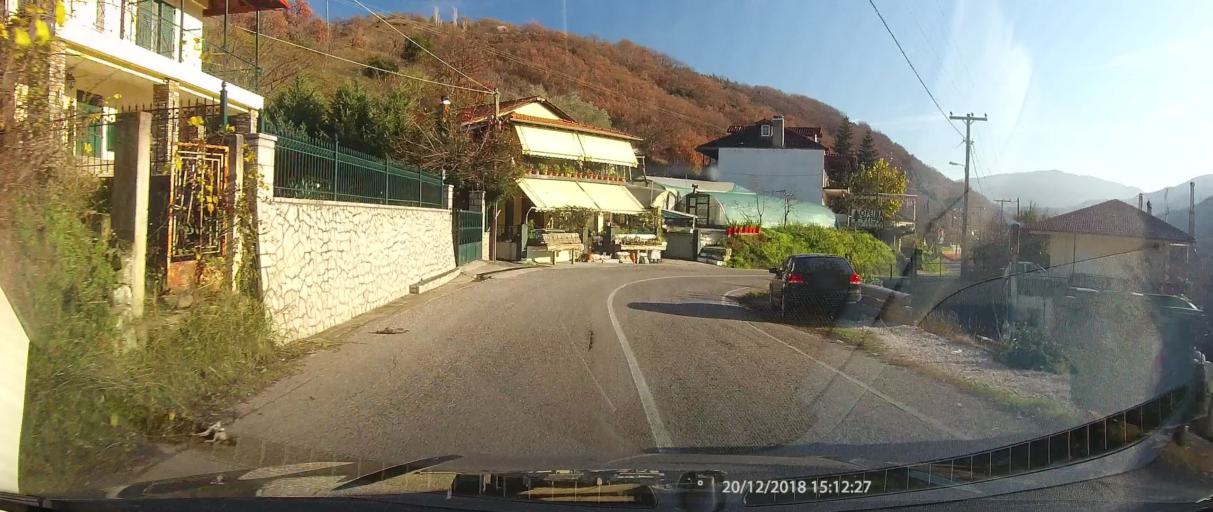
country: GR
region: Central Greece
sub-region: Nomos Fthiotidos
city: Makrakomi
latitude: 38.9422
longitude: 21.9628
